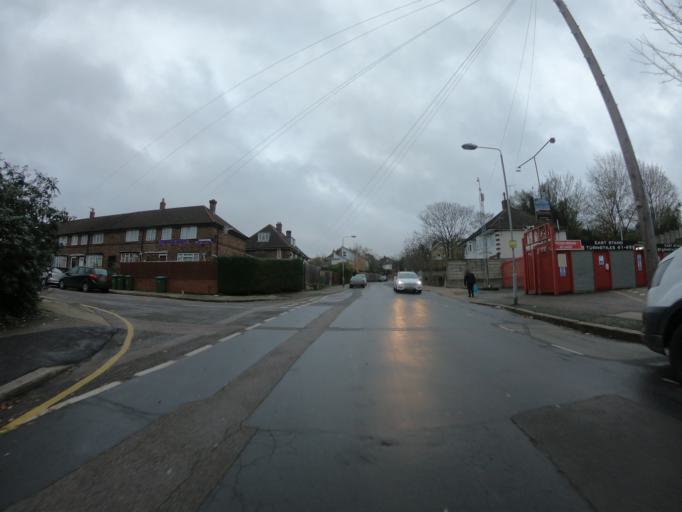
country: GB
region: England
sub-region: Greater London
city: Woolwich
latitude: 51.4873
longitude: 0.0377
